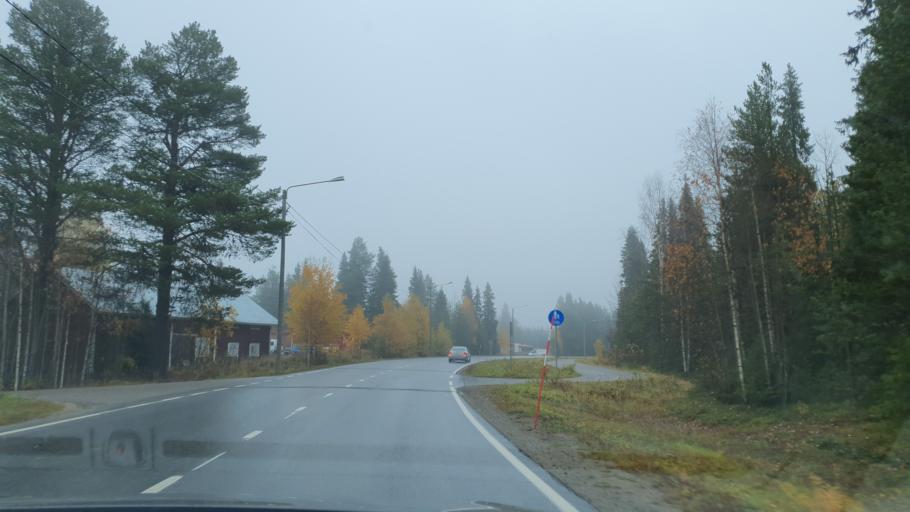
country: FI
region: Lapland
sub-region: Tunturi-Lappi
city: Kittilae
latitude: 67.6709
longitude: 24.8724
